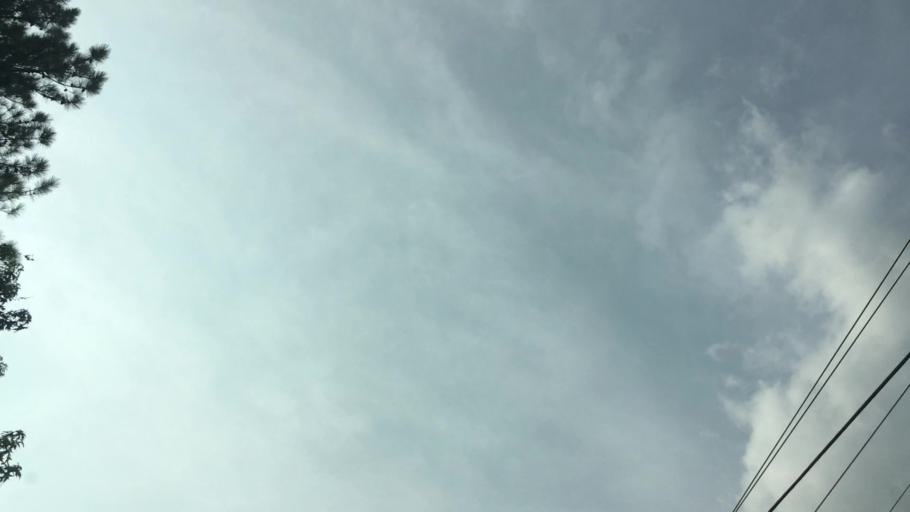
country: US
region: Alabama
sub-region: Bibb County
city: Woodstock
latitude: 33.2233
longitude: -87.1239
